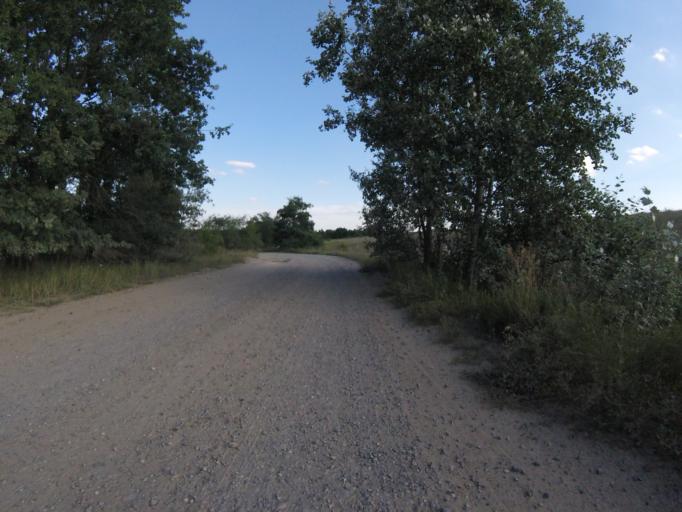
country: DE
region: Brandenburg
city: Zossen
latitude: 52.2127
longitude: 13.4798
